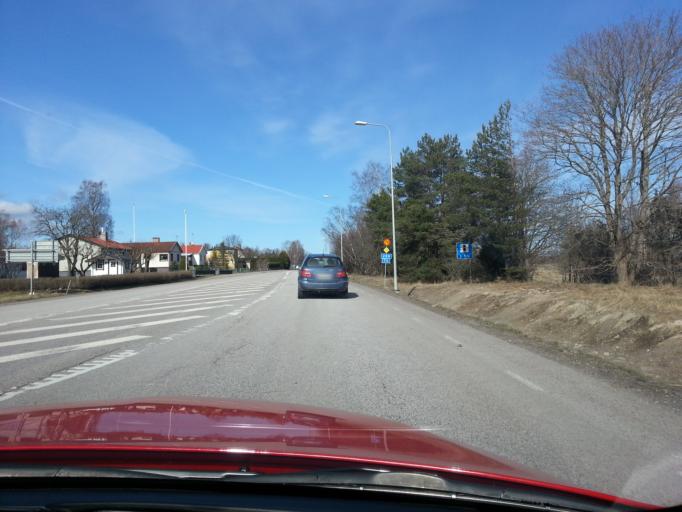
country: SE
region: Uppsala
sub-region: Osthammars Kommun
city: Gimo
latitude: 60.1650
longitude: 18.1938
